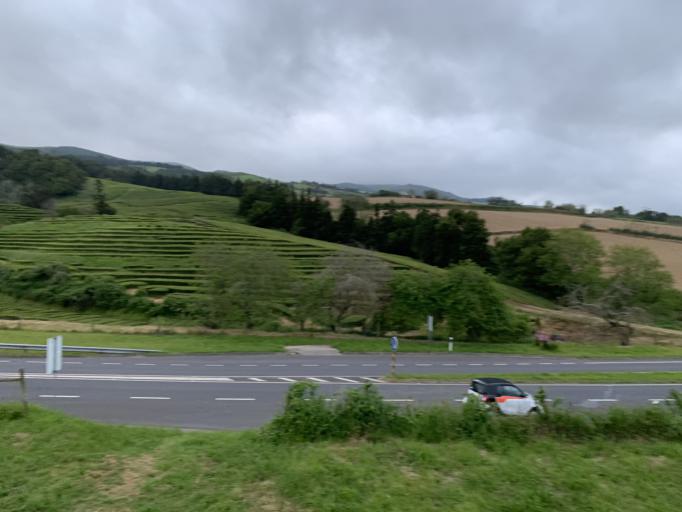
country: PT
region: Azores
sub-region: Povoacao
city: Furnas
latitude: 37.8170
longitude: -25.4019
